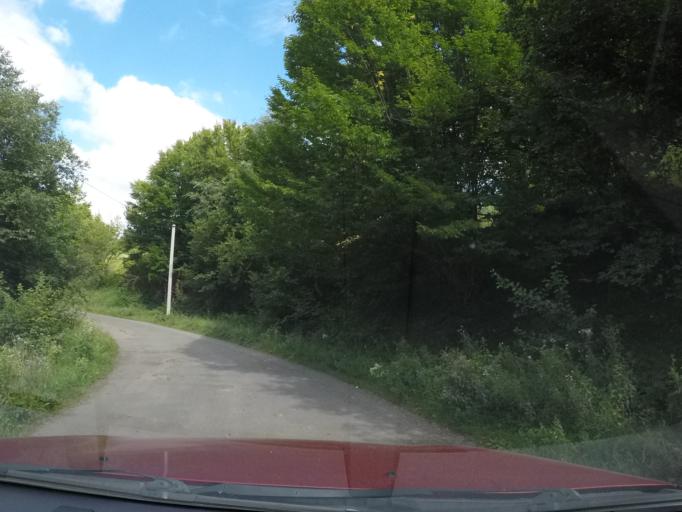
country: UA
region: Zakarpattia
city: Velykyi Bereznyi
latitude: 48.9480
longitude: 22.6772
